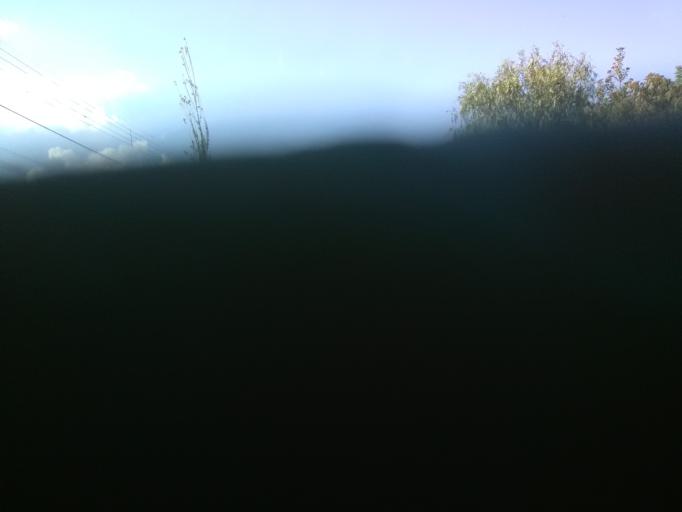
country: BO
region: Cochabamba
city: Cochabamba
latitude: -17.3624
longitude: -66.2126
